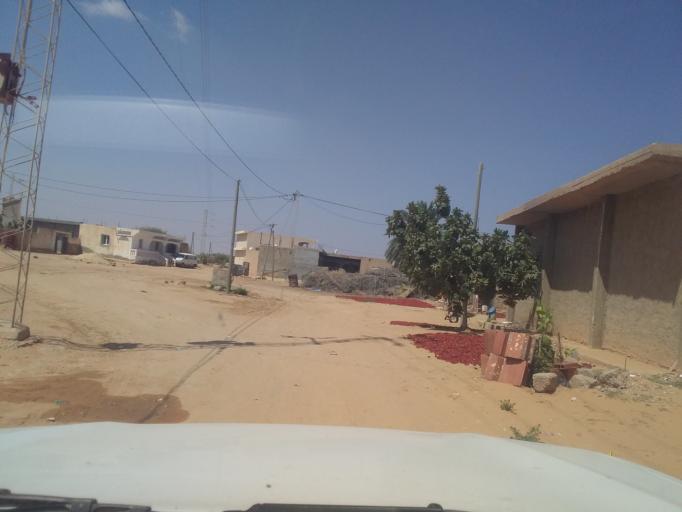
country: TN
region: Qabis
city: Matmata
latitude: 33.5942
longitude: 10.2848
